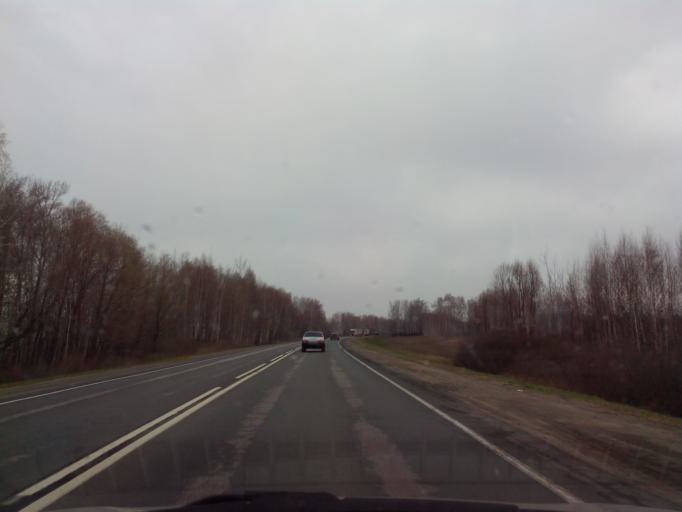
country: RU
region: Tambov
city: Pervomayskiy
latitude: 53.0889
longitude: 40.4006
